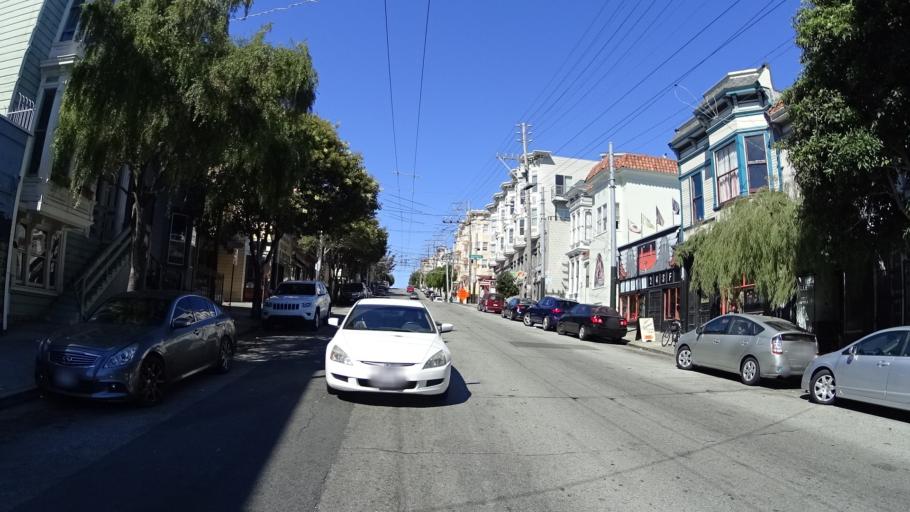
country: US
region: California
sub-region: San Francisco County
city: San Francisco
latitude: 37.7714
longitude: -122.4303
